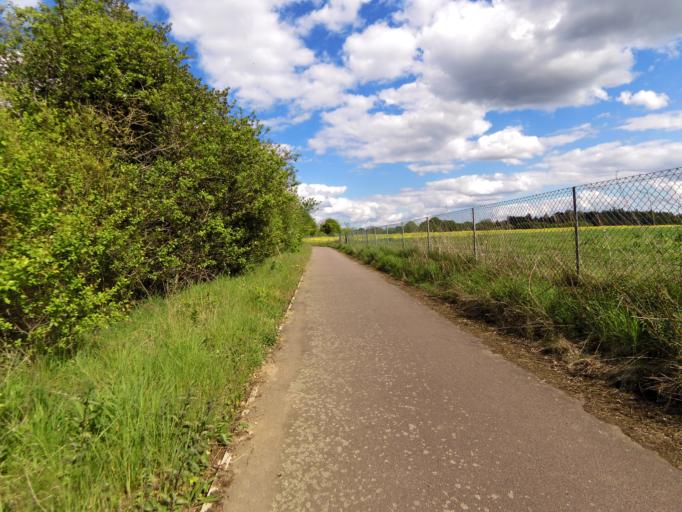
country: GB
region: England
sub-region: Suffolk
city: Great Barton
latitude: 52.2483
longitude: 0.7766
